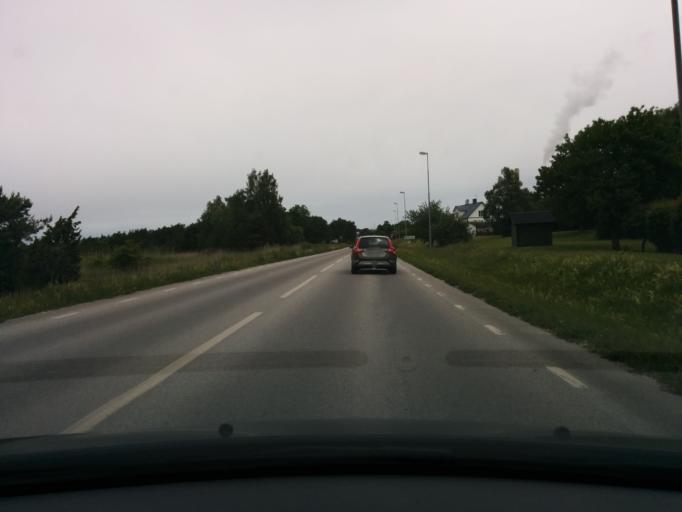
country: SE
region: Gotland
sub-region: Gotland
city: Slite
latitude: 57.7007
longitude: 18.7951
